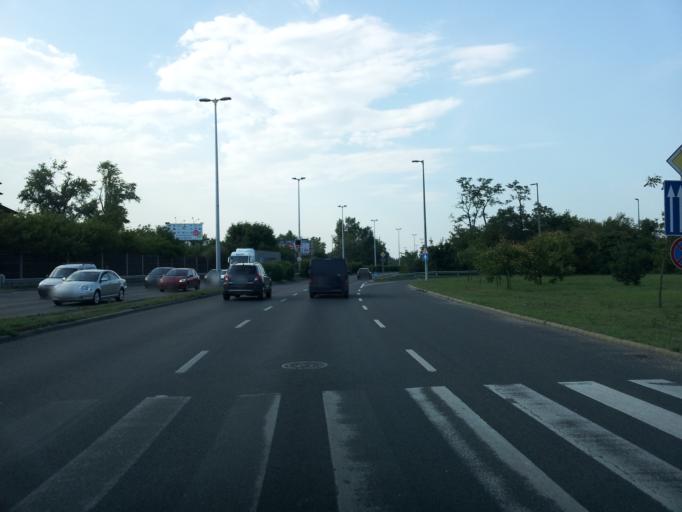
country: HU
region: Budapest
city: Budapest XX. keruelet
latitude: 47.4657
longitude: 19.1047
